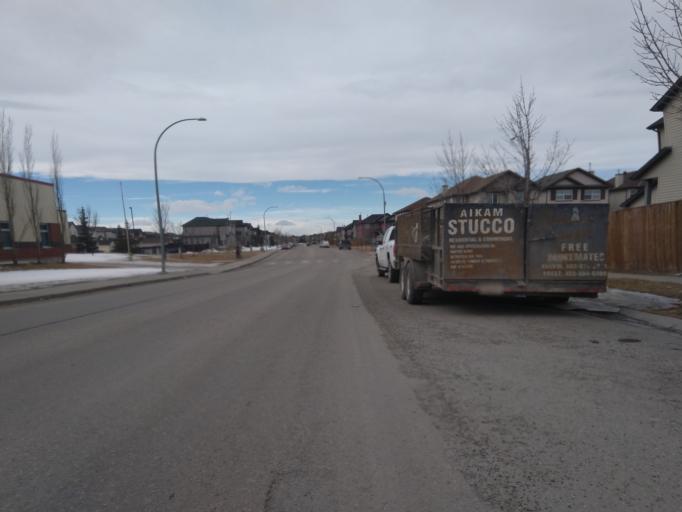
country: CA
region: Alberta
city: Chestermere
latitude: 51.1374
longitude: -113.9364
